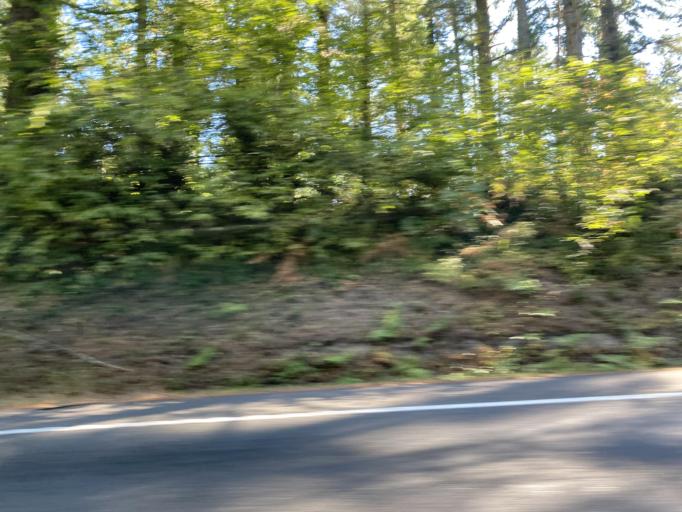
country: US
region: Washington
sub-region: Thurston County
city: Rainier
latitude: 46.9136
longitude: -122.7356
